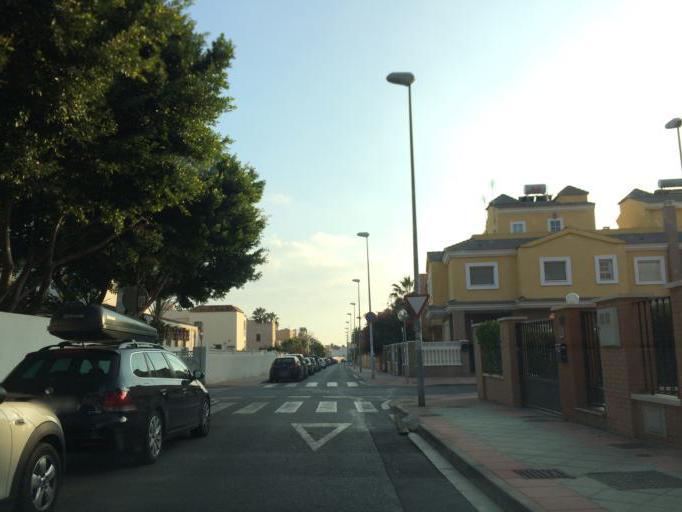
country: ES
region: Andalusia
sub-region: Provincia de Almeria
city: Almeria
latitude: 36.8239
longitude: -2.4373
